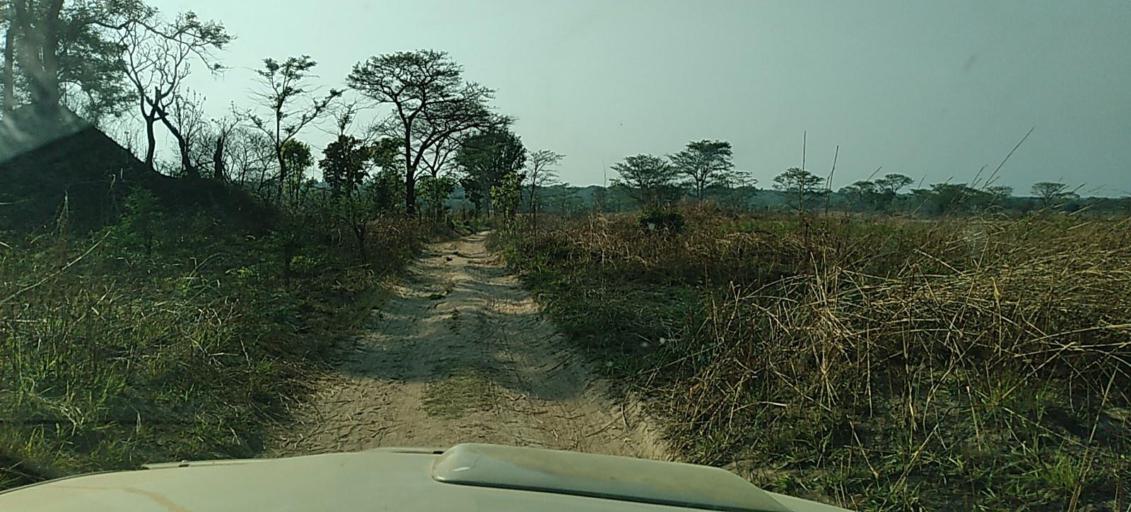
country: ZM
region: North-Western
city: Kasempa
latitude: -13.1866
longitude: 25.9667
